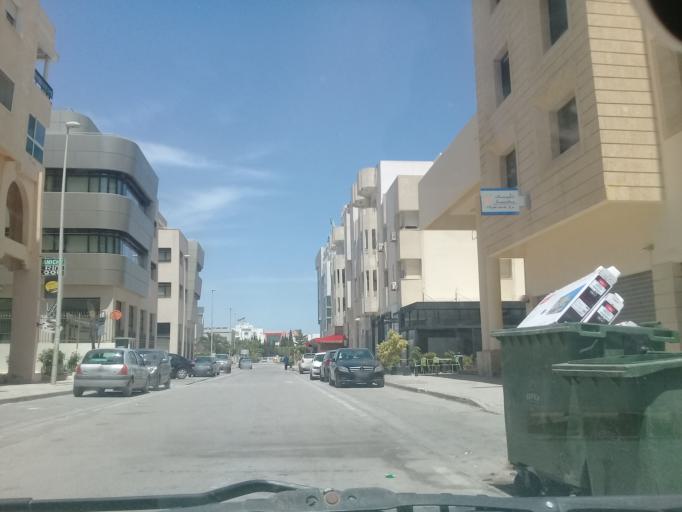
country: TN
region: Ariana
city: Ariana
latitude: 36.8343
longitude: 10.2413
